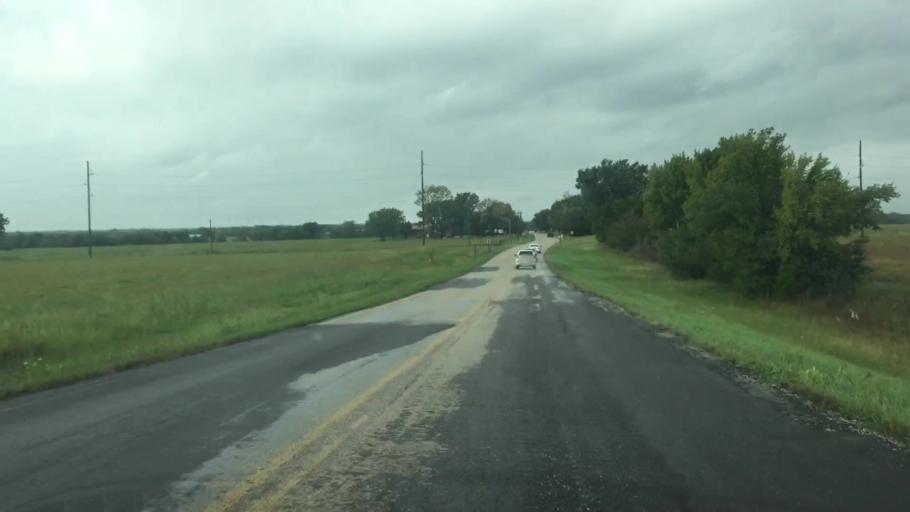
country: US
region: Kansas
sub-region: Allen County
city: Iola
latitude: 37.8857
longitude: -95.4163
